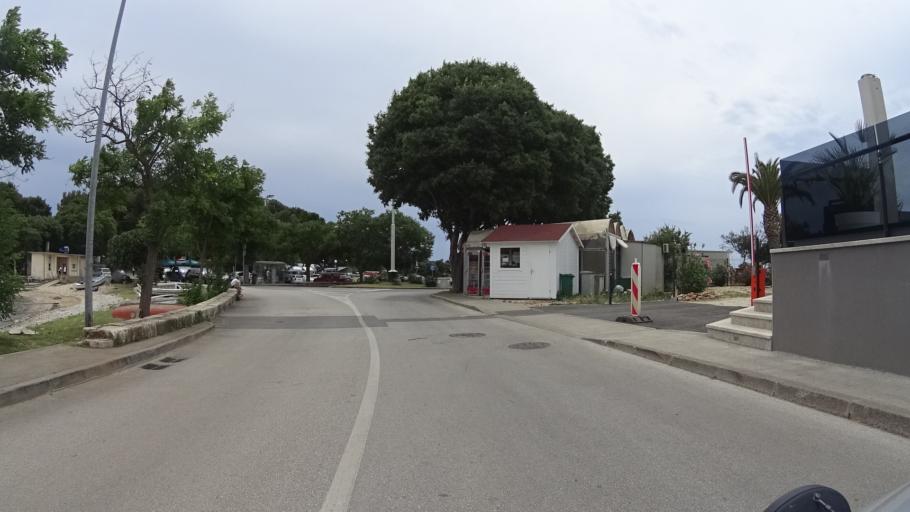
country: HR
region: Istarska
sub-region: Grad Pula
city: Pula
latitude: 44.8604
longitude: 13.8150
